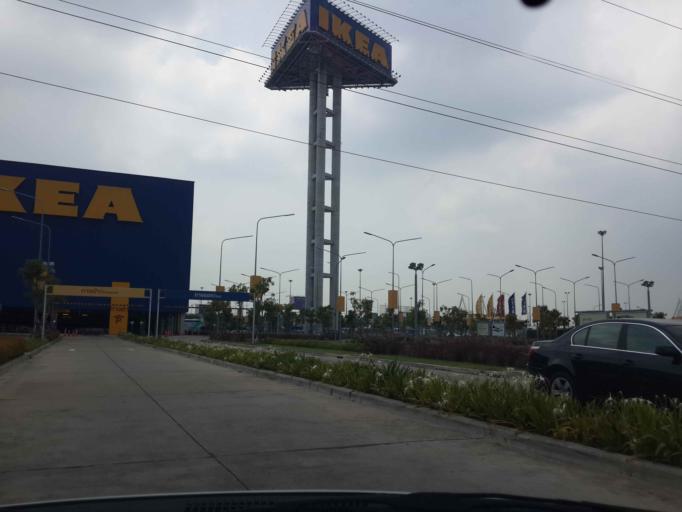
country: TH
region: Bangkok
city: Bang Na
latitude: 13.6430
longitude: 100.6794
